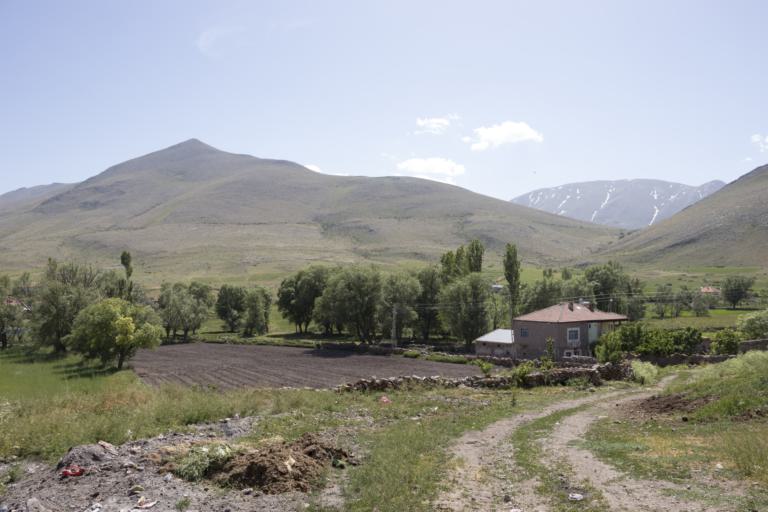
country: TR
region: Kayseri
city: Toklar
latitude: 38.4217
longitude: 36.0944
